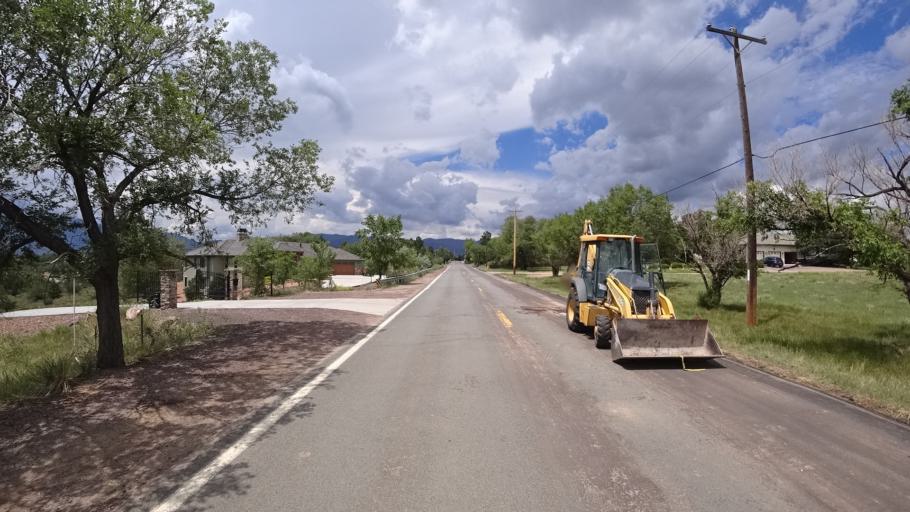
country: US
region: Colorado
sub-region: El Paso County
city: Colorado Springs
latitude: 38.8563
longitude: -104.8456
